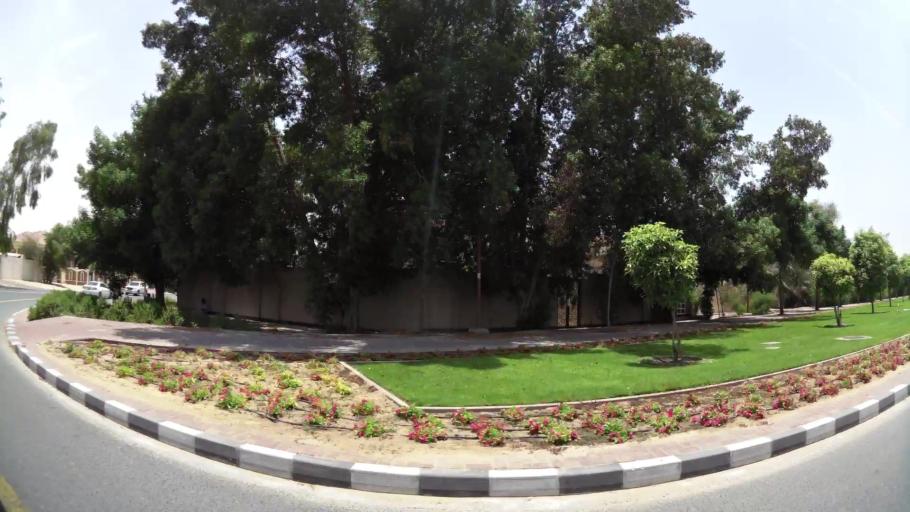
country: AE
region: Ash Shariqah
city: Sharjah
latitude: 25.2130
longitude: 55.3827
